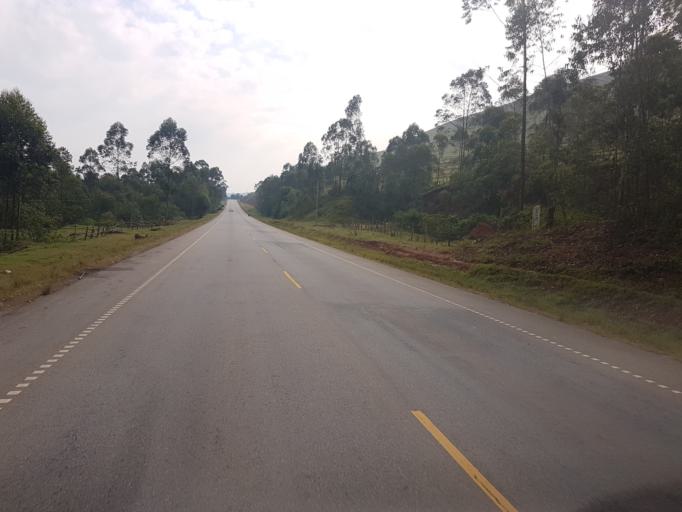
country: UG
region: Western Region
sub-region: Ntungamo District
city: Ntungamo
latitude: -0.7951
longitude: 30.2659
